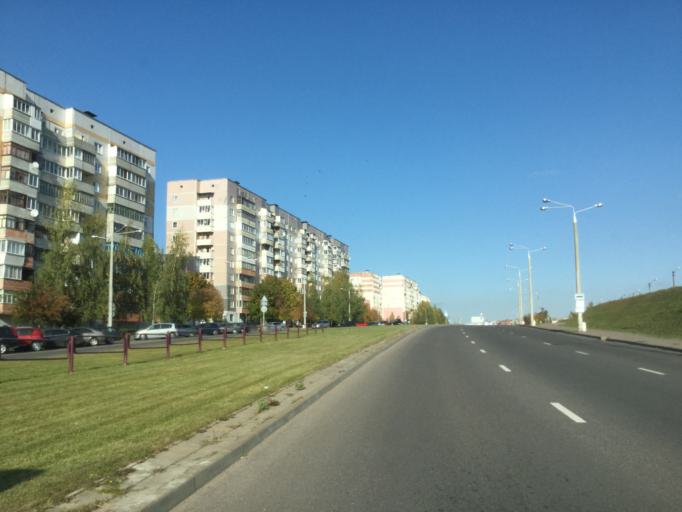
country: BY
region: Vitebsk
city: Vitebsk
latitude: 55.1555
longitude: 30.2111
